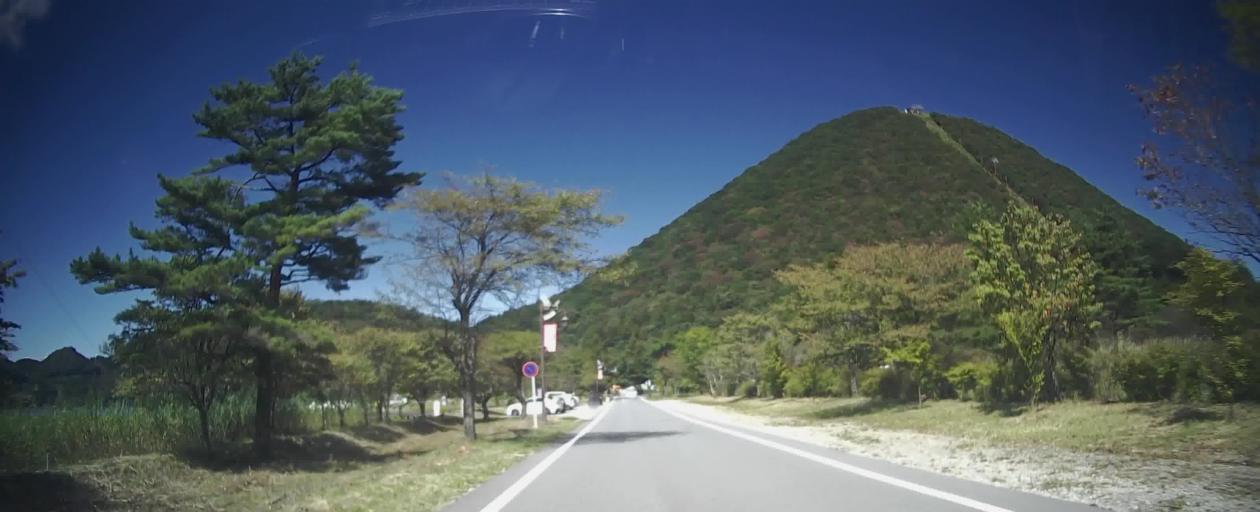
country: JP
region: Gunma
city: Nakanojomachi
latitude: 36.4693
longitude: 138.8736
